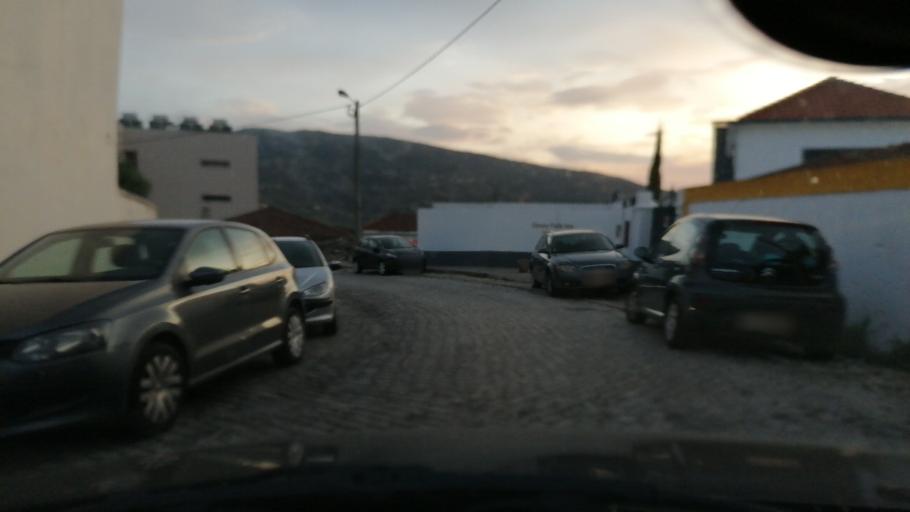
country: PT
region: Vila Real
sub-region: Peso da Regua
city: Peso da Regua
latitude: 41.1623
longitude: -7.7867
